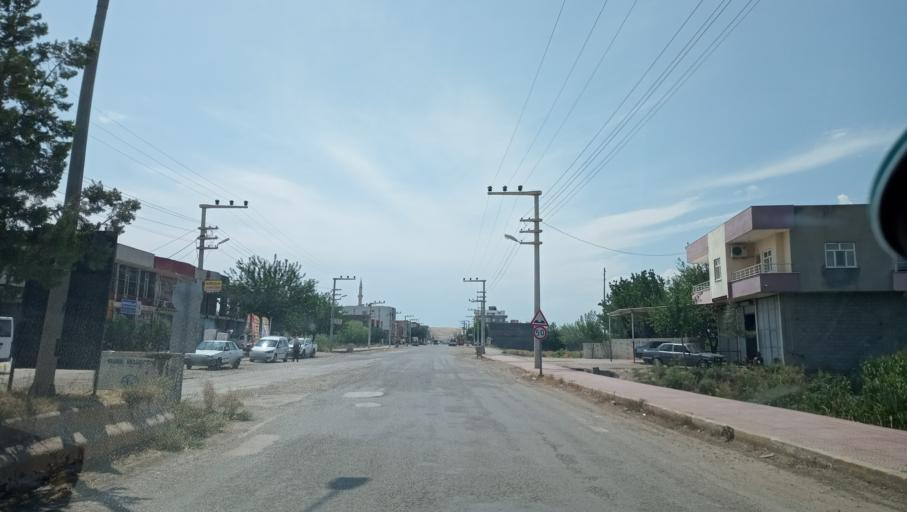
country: TR
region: Diyarbakir
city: Tepe
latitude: 37.7925
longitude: 40.7701
